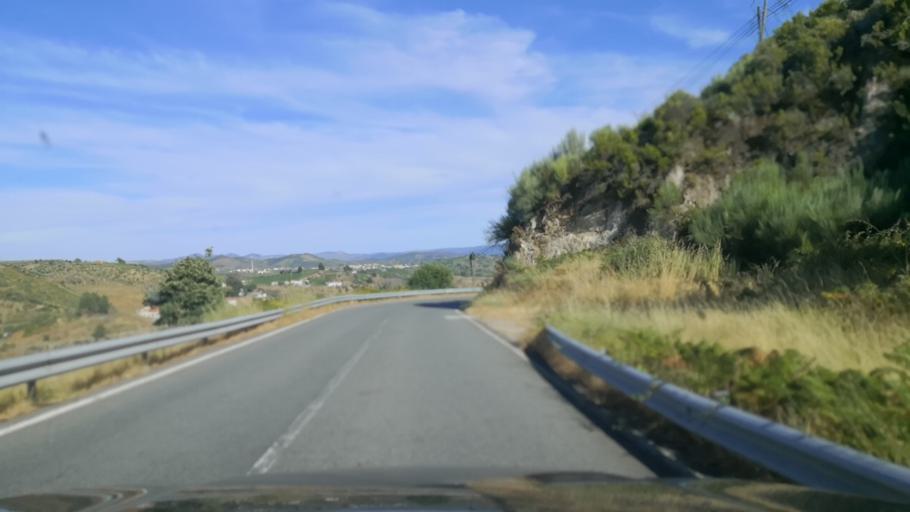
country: PT
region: Vila Real
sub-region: Murca
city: Murca
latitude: 41.4033
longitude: -7.4723
